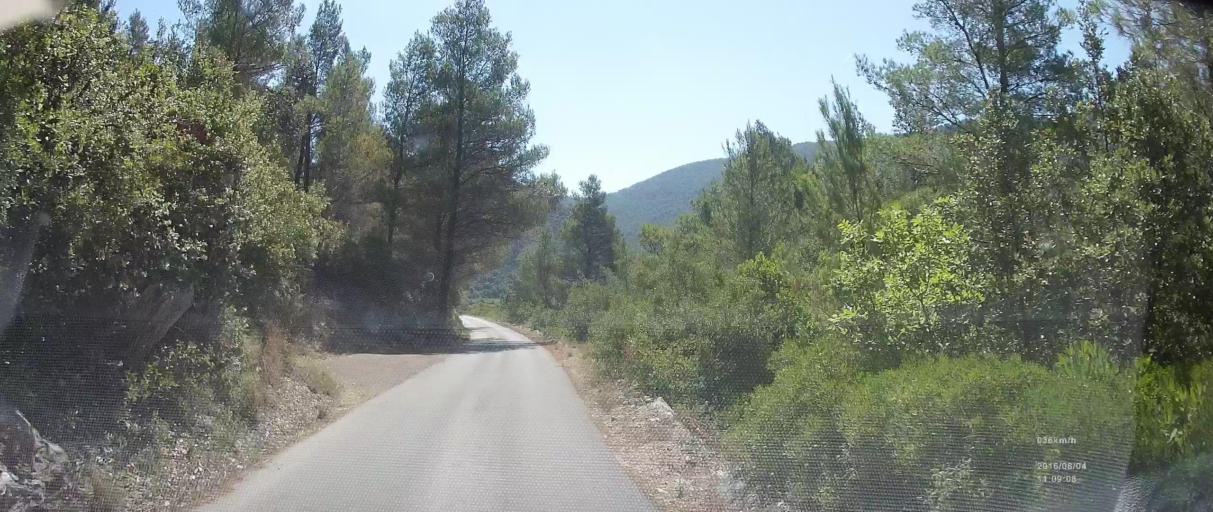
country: HR
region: Dubrovacko-Neretvanska
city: Blato
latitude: 42.7639
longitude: 17.4744
